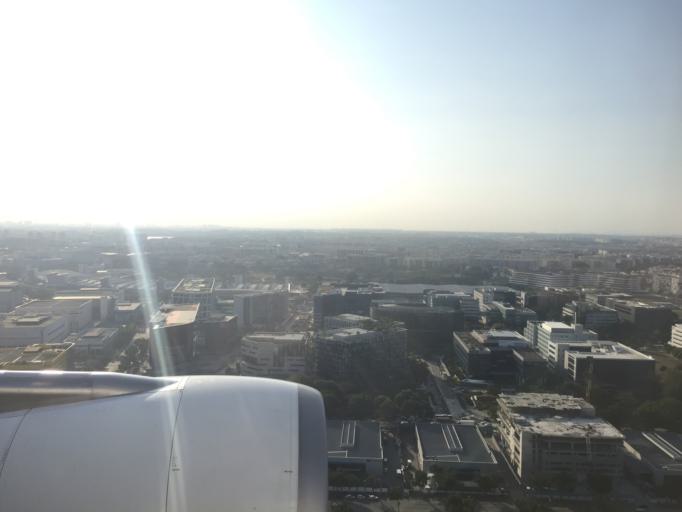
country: SG
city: Singapore
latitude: 1.3312
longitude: 103.9698
